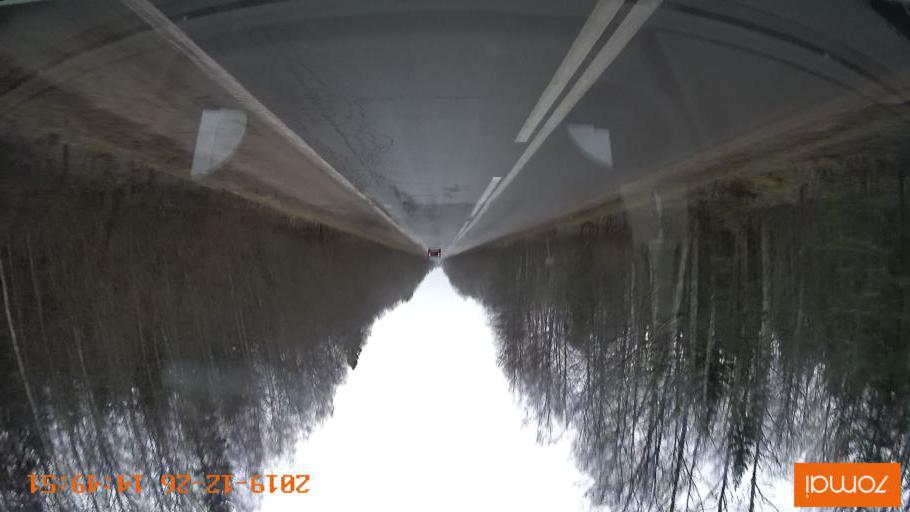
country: RU
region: Jaroslavl
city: Poshekhon'ye
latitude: 58.3367
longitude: 38.9364
